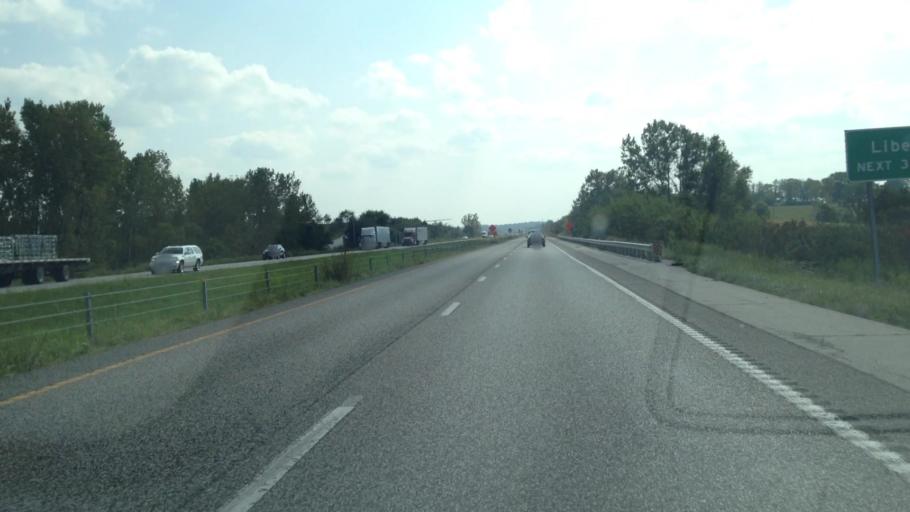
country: US
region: Missouri
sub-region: Clay County
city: Liberty
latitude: 39.2980
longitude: -94.4101
